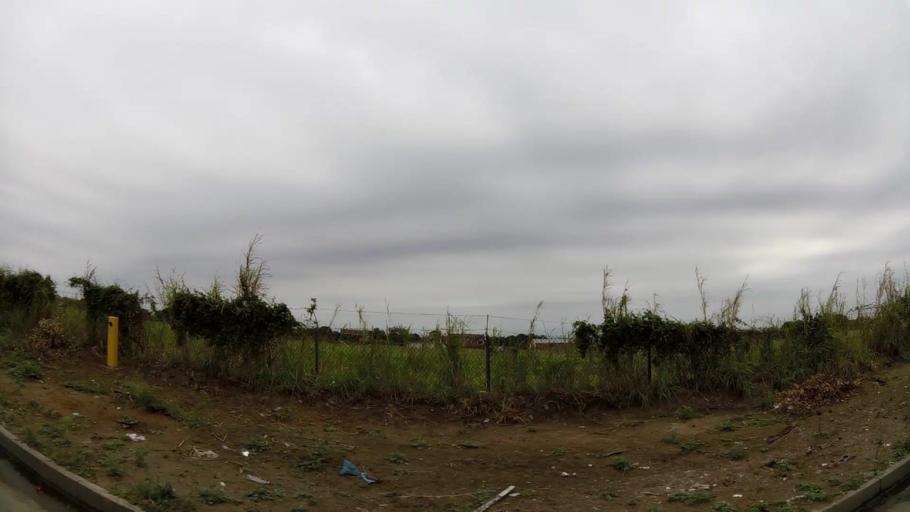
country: BO
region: Santa Cruz
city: Santa Cruz de la Sierra
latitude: -17.8125
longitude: -63.1695
